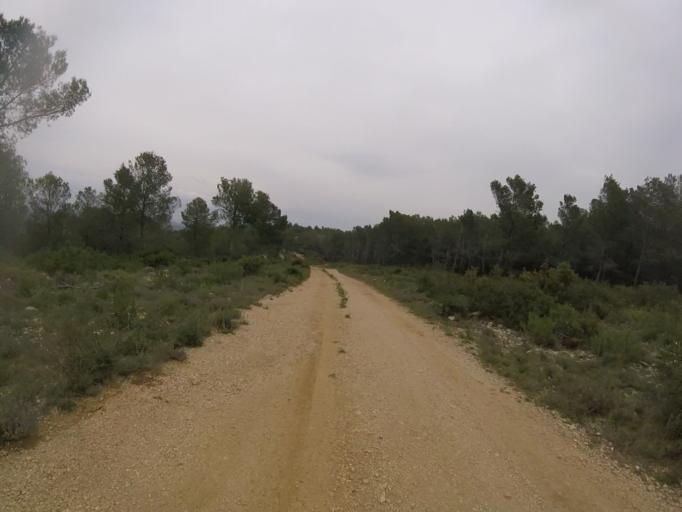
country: ES
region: Valencia
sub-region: Provincia de Castello
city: Alcala de Xivert
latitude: 40.3162
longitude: 0.2692
